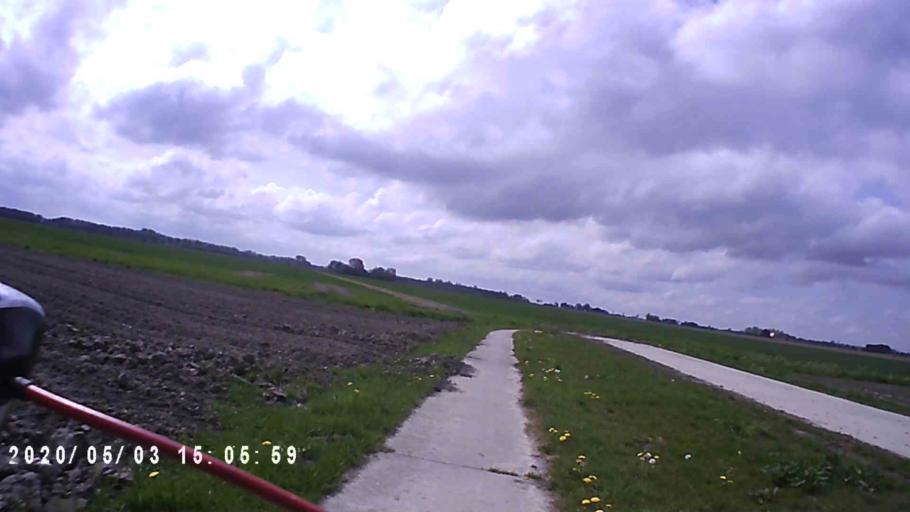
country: NL
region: Groningen
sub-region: Gemeente Zuidhorn
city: Oldehove
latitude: 53.3715
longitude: 6.4415
